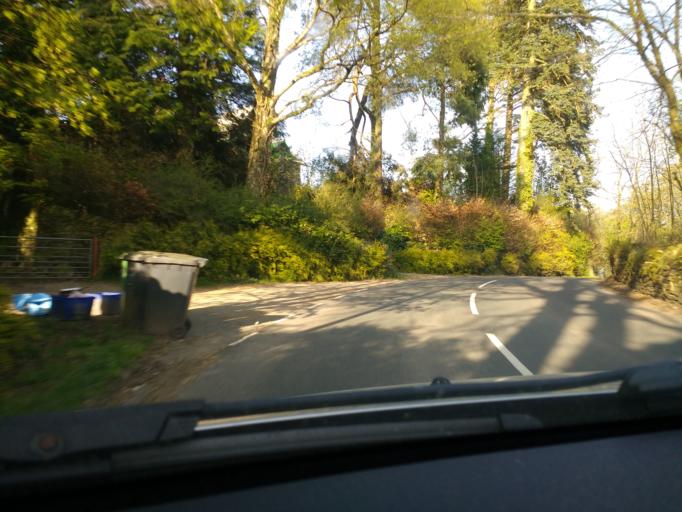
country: GB
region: England
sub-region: Cumbria
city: Sedbergh
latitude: 54.3008
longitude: -2.3961
